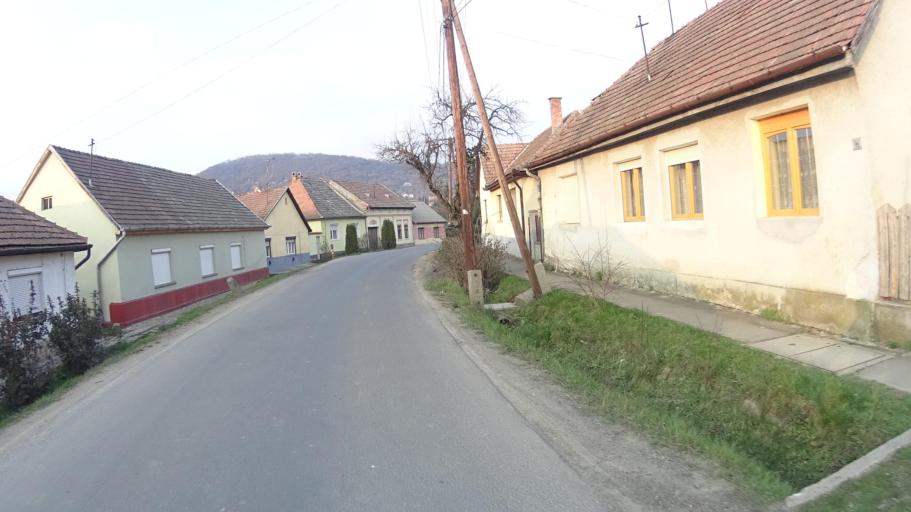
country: HU
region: Pest
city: Veroce
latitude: 47.8276
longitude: 19.0378
